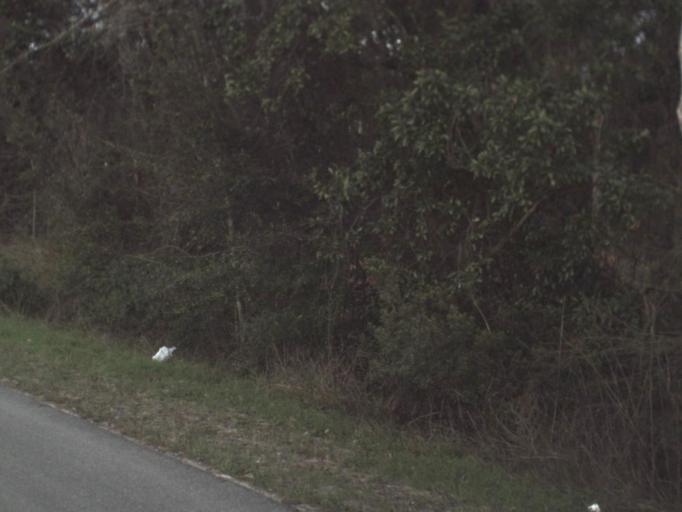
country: US
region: Florida
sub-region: Bay County
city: Cedar Grove
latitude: 30.1859
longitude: -85.6249
